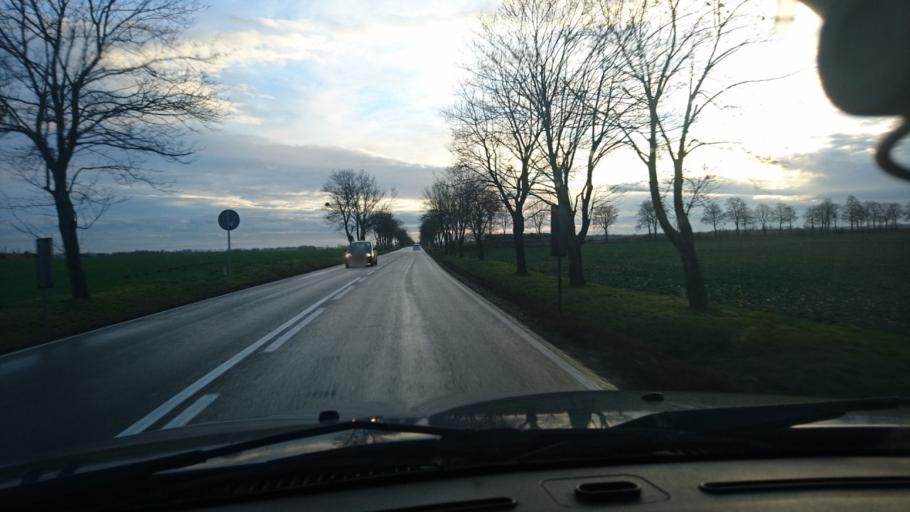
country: PL
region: Opole Voivodeship
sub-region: Powiat kluczborski
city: Byczyna
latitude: 51.0974
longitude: 18.2038
